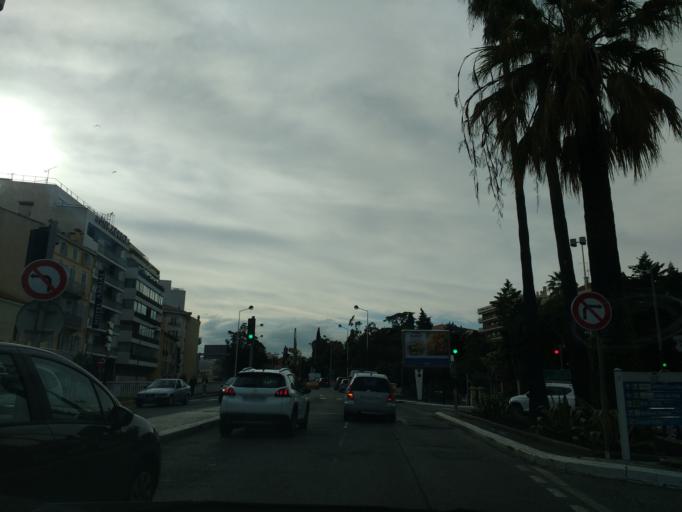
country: FR
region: Provence-Alpes-Cote d'Azur
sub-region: Departement des Alpes-Maritimes
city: Cannes
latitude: 43.5530
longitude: 7.0280
